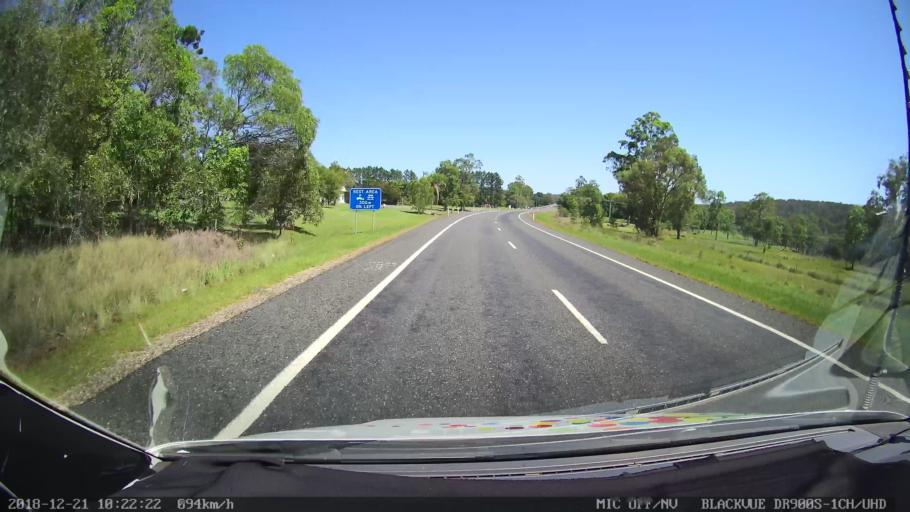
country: AU
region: New South Wales
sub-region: Clarence Valley
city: South Grafton
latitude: -29.6549
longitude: 152.8015
